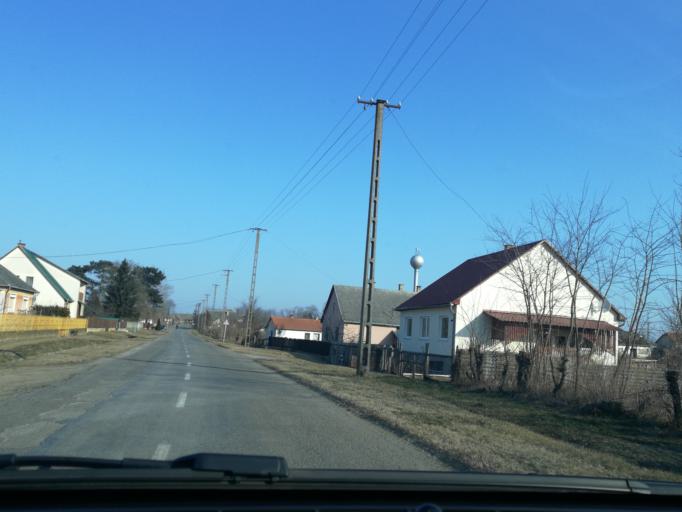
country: HU
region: Szabolcs-Szatmar-Bereg
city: Nyirbogdany
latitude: 48.0525
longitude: 21.9360
